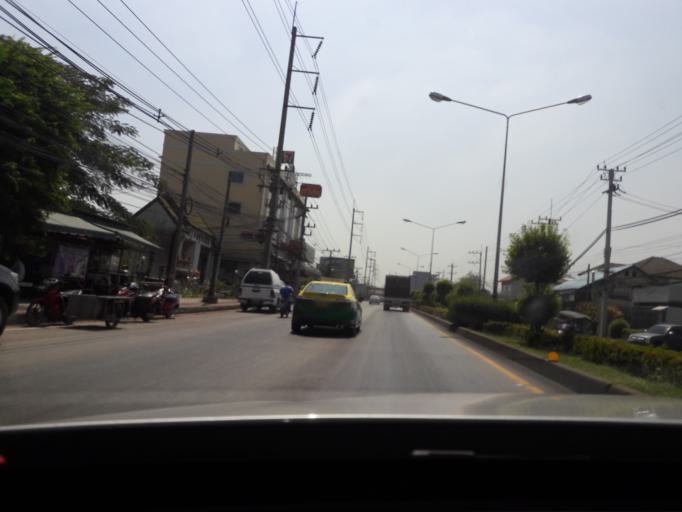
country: TH
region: Samut Sakhon
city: Samut Sakhon
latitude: 13.5849
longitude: 100.2786
